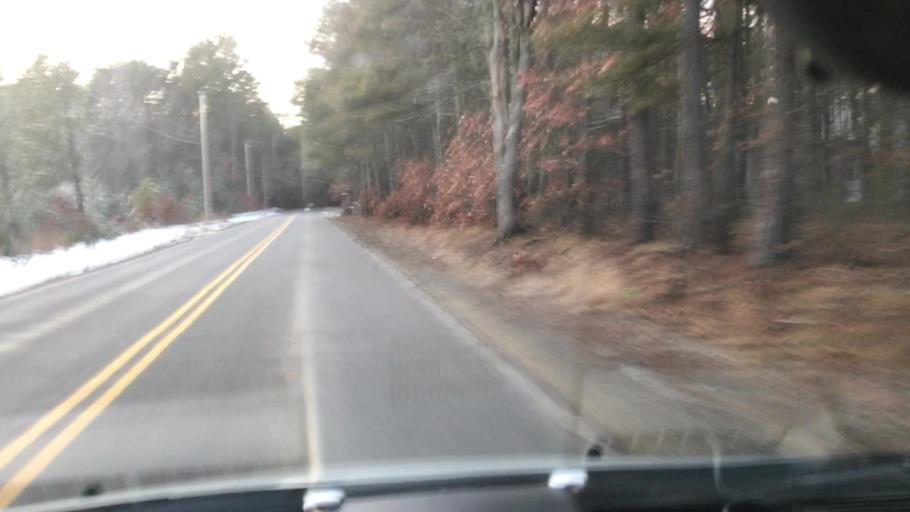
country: US
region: New Hampshire
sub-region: Hillsborough County
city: Merrimack
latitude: 42.8383
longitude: -71.5655
